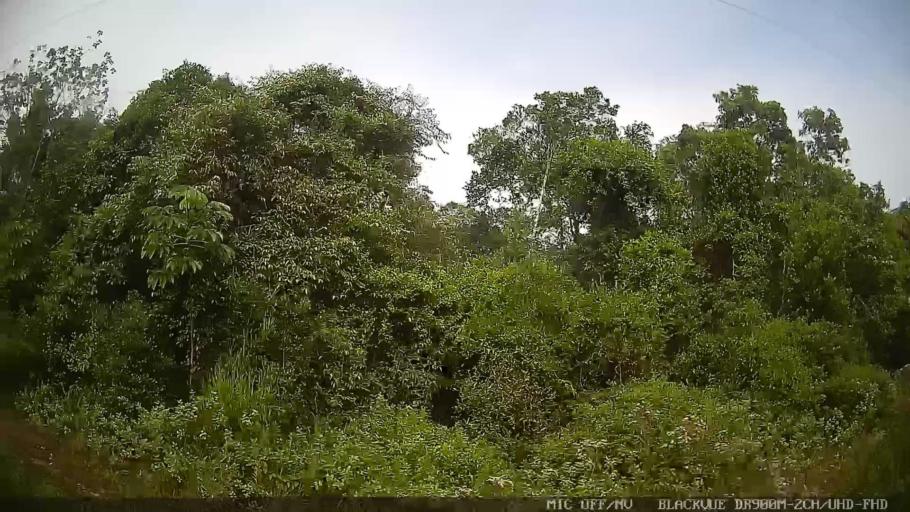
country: BR
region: Sao Paulo
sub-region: Peruibe
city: Peruibe
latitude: -24.2187
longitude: -46.9291
